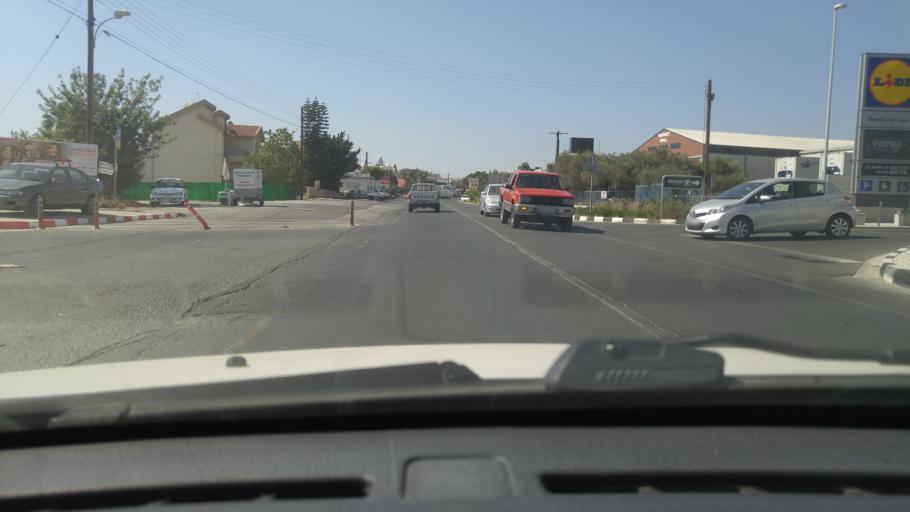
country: CY
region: Limassol
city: Ypsonas
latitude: 34.6821
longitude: 32.9719
